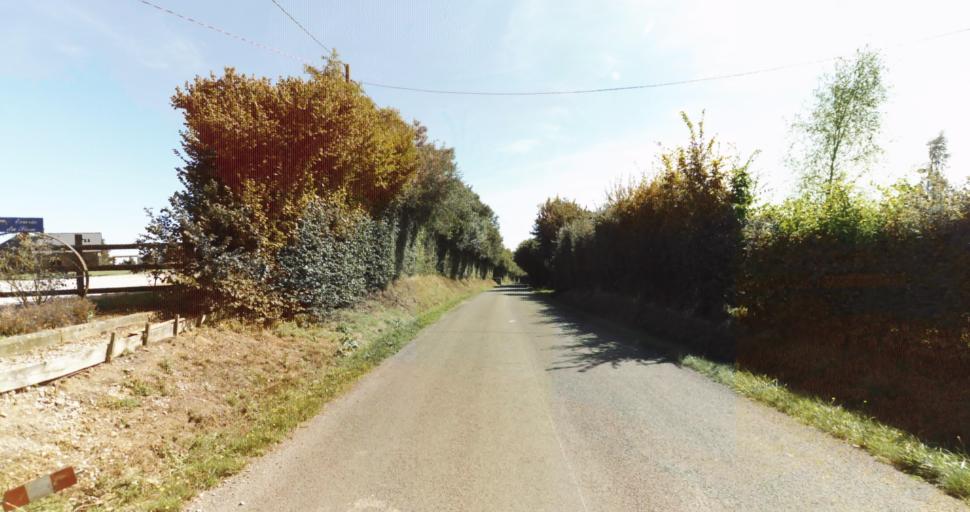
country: FR
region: Lower Normandy
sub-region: Departement de l'Orne
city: Gace
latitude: 48.7620
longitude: 0.2552
